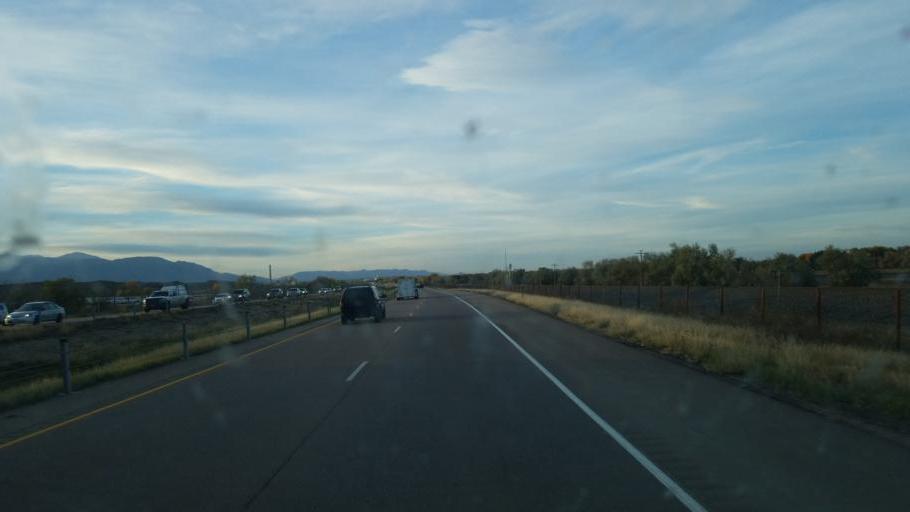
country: US
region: Colorado
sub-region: El Paso County
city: Fountain
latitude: 38.6017
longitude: -104.6772
